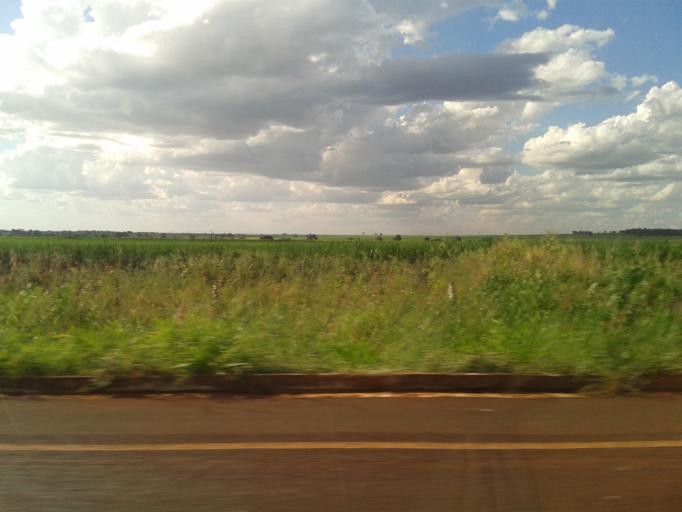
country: BR
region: Minas Gerais
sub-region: Santa Vitoria
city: Santa Vitoria
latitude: -18.6949
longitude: -49.9273
